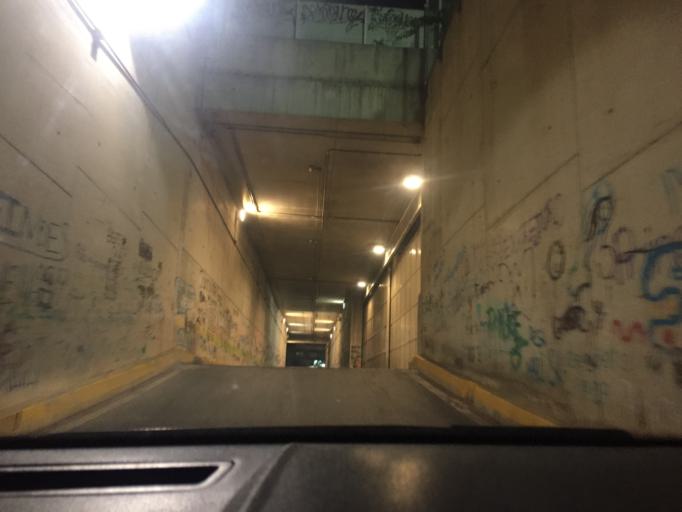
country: ES
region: Andalusia
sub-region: Provincia de Jaen
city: Jaen
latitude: 37.7767
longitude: -3.7868
